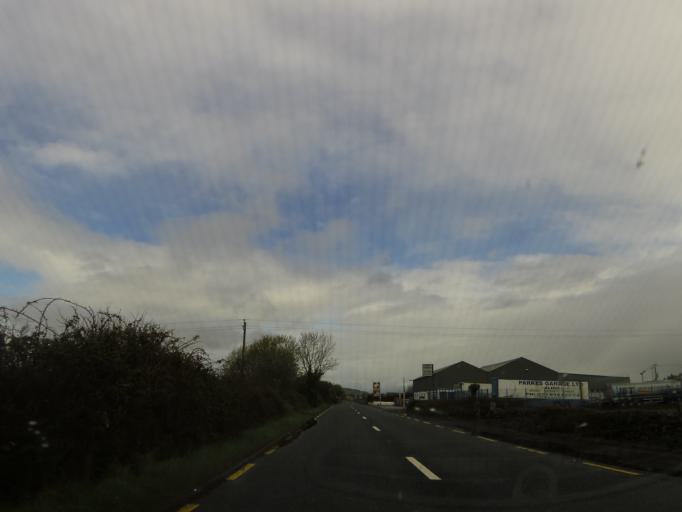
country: IE
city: Ballisodare
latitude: 54.2014
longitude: -8.5001
